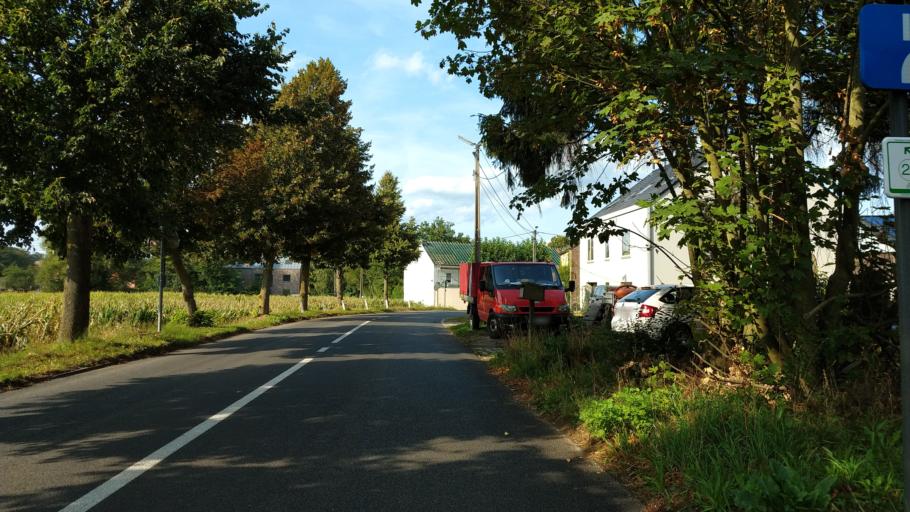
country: BE
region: Flanders
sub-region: Provincie Vlaams-Brabant
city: Lubbeek
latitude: 50.8605
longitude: 4.8219
